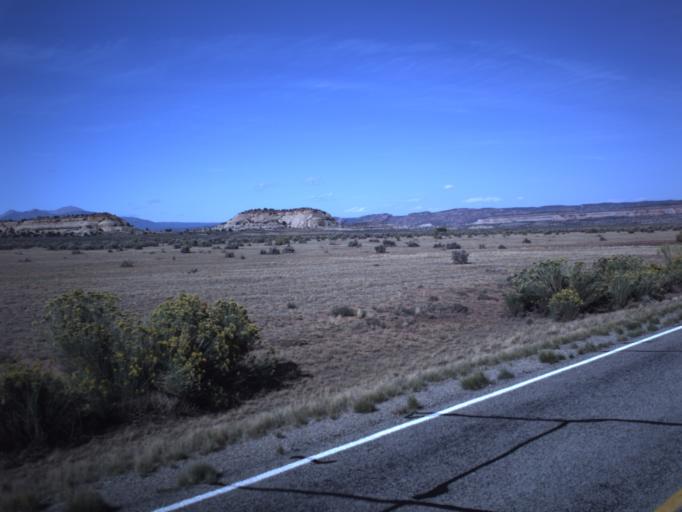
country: US
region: Utah
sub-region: San Juan County
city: Monticello
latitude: 38.0655
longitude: -109.3826
